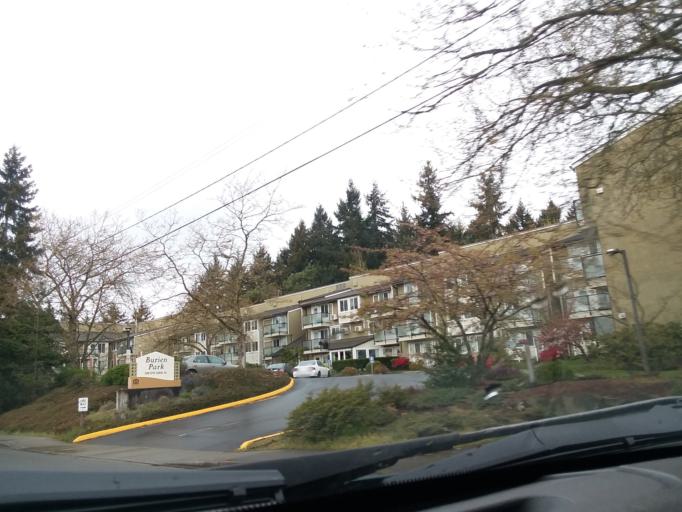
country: US
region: Washington
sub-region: King County
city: Burien
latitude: 47.4705
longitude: -122.3394
